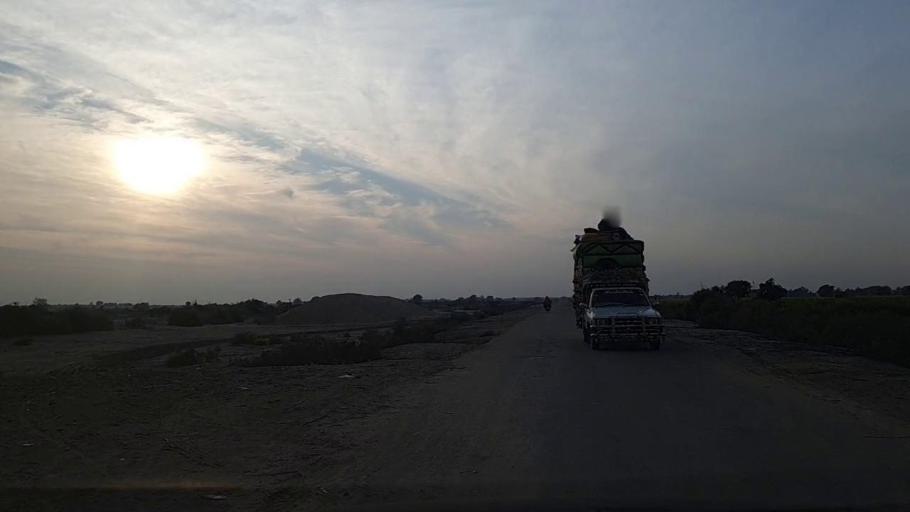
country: PK
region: Sindh
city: Jam Sahib
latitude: 26.4028
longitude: 68.4983
